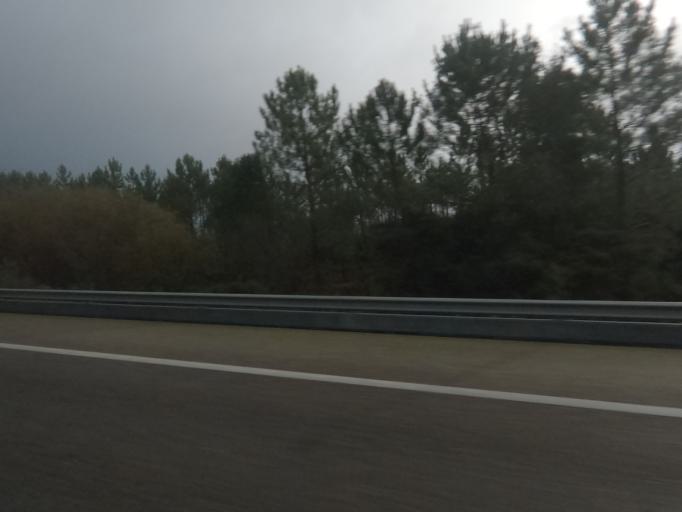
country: PT
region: Viana do Castelo
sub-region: Ponte de Lima
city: Ponte de Lima
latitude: 41.8175
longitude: -8.5997
